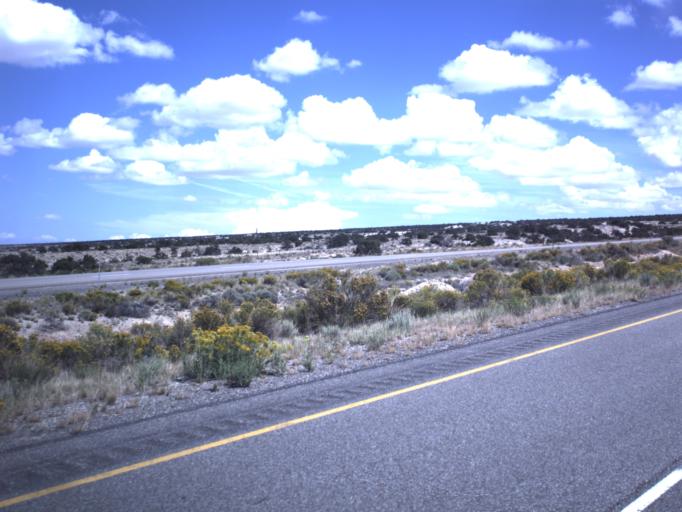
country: US
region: Utah
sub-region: Emery County
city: Ferron
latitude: 38.8417
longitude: -110.9644
